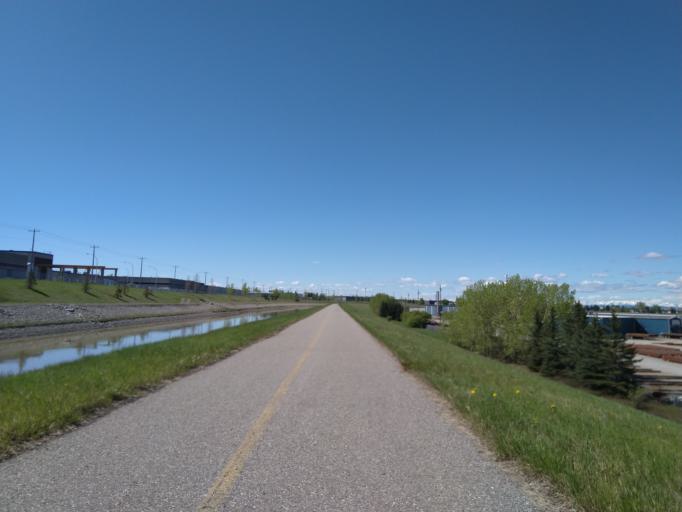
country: CA
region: Alberta
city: Calgary
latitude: 50.9893
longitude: -113.9873
